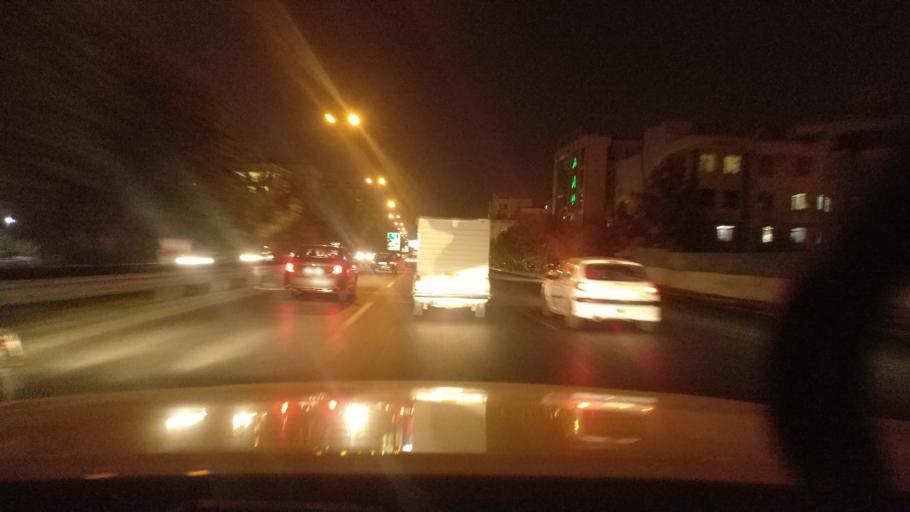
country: IR
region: Tehran
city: Tehran
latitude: 35.7236
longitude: 51.3092
